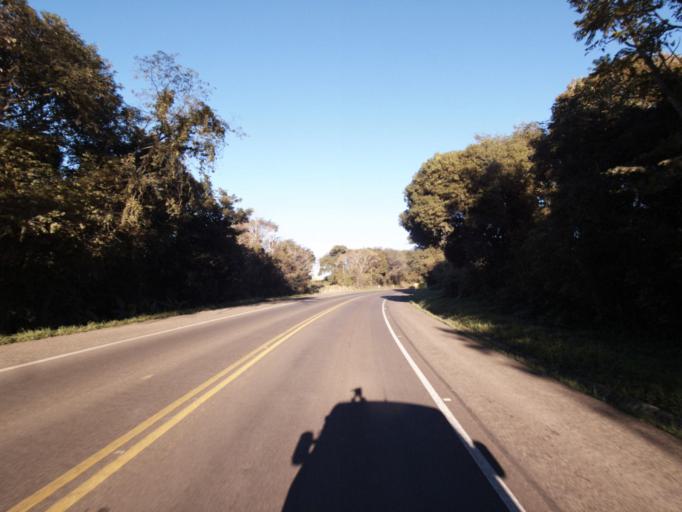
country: BR
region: Rio Grande do Sul
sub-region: Frederico Westphalen
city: Frederico Westphalen
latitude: -26.7828
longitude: -53.2782
